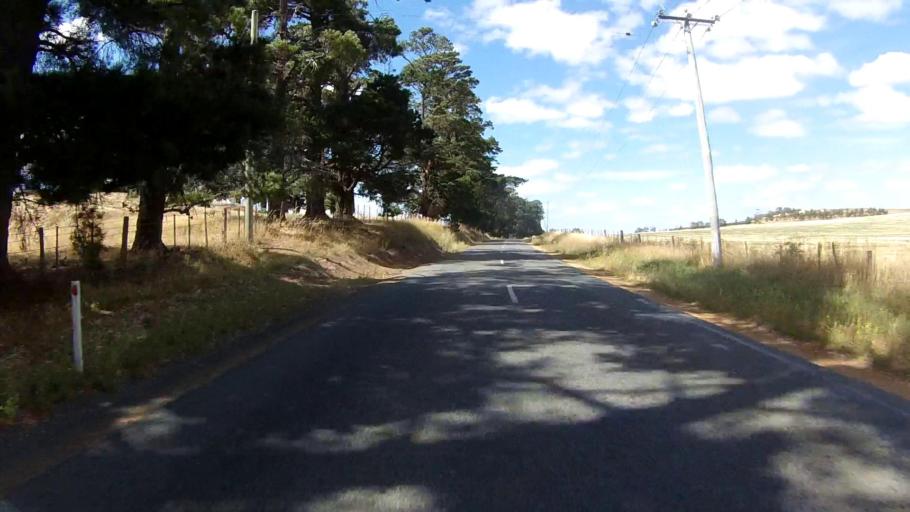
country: AU
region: Tasmania
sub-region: Sorell
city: Sorell
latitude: -42.6375
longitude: 147.4323
